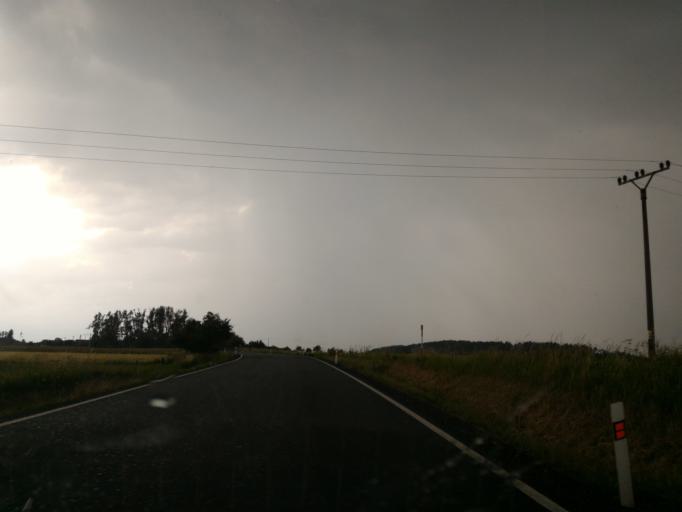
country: CZ
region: Vysocina
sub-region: Okres Jihlava
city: Telc
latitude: 49.1490
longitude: 15.5398
